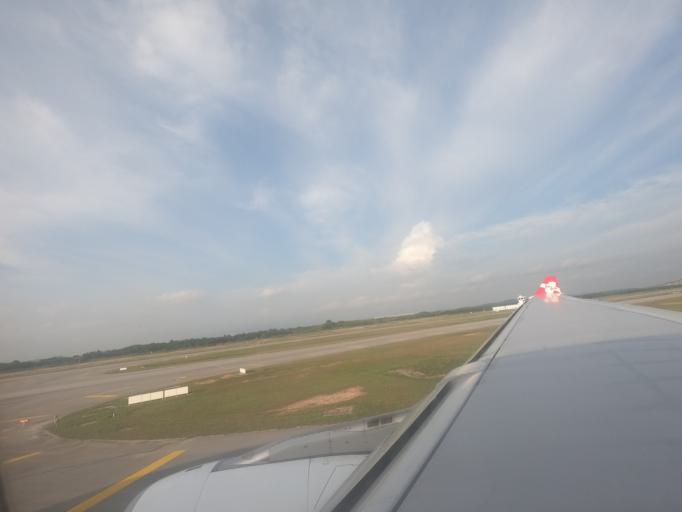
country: MY
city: Sungai Pelek New Village
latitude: 2.7266
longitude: 101.6862
